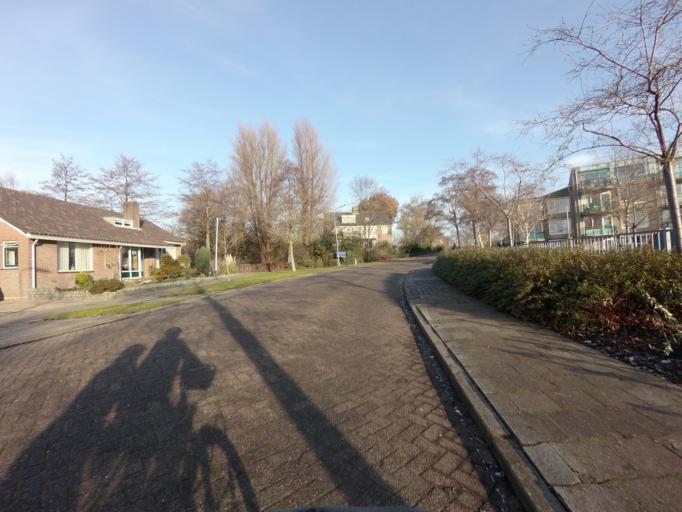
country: NL
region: Utrecht
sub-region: Gemeente De Ronde Venen
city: Mijdrecht
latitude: 52.2071
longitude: 4.8621
